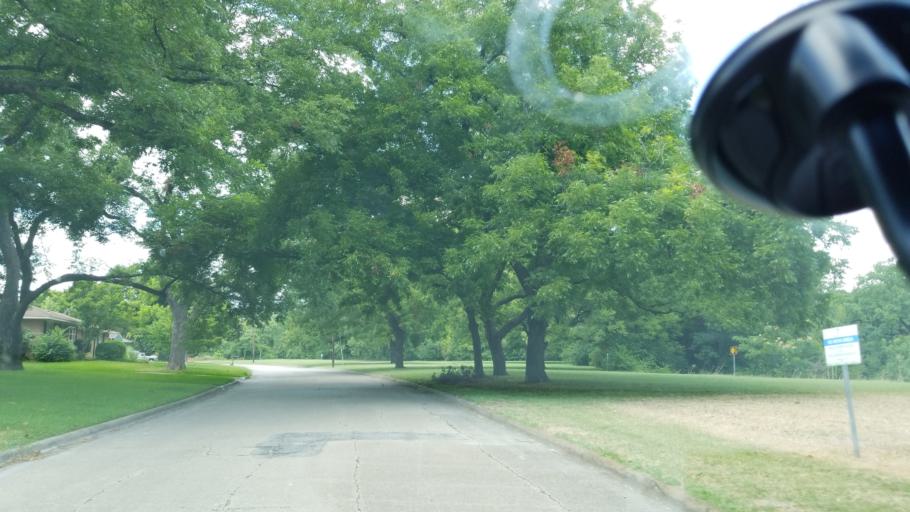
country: US
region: Texas
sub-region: Dallas County
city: Cockrell Hill
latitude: 32.7018
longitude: -96.8524
